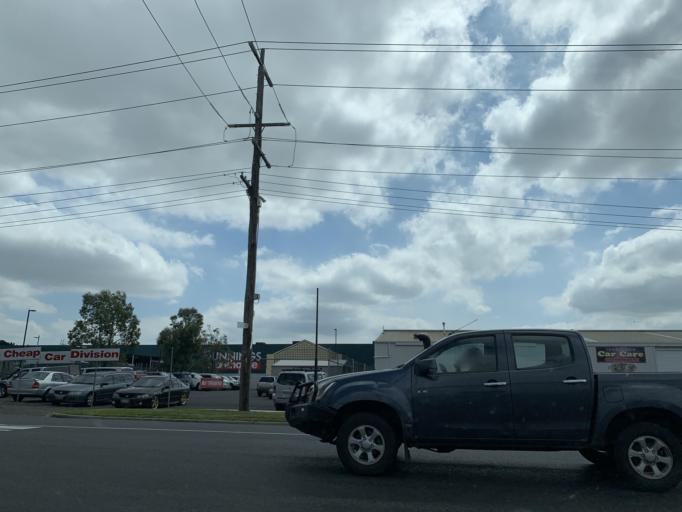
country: AU
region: Victoria
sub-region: Latrobe
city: Traralgon
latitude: -38.1918
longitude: 146.5622
